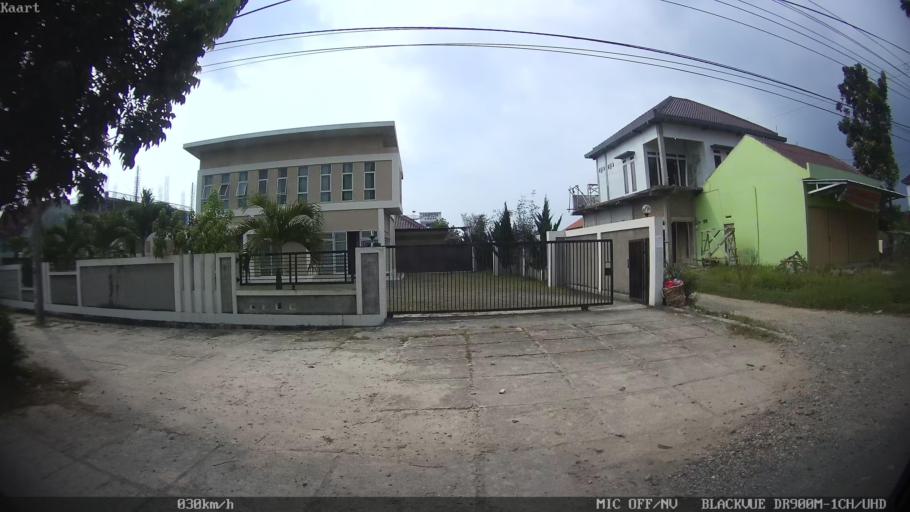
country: ID
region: Lampung
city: Gadingrejo
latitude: -5.3742
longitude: 105.0419
